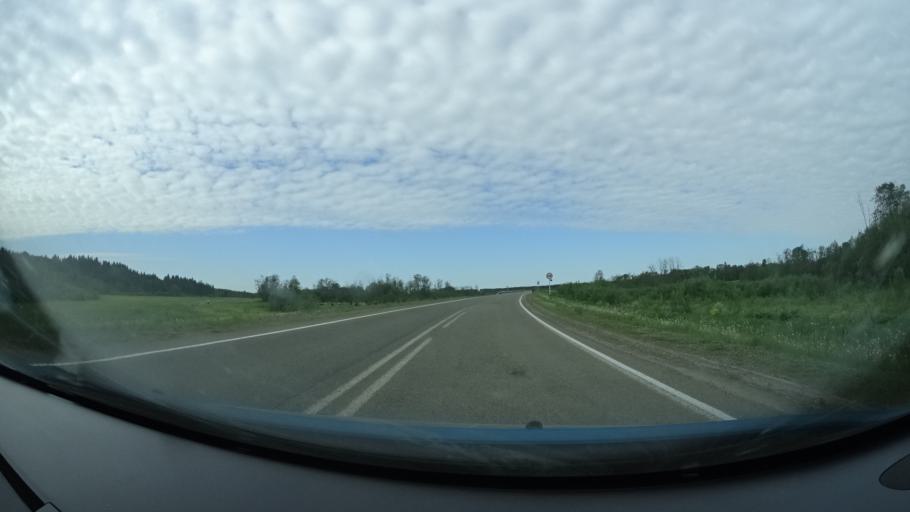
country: RU
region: Perm
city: Kuyeda
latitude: 56.5037
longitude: 55.6247
